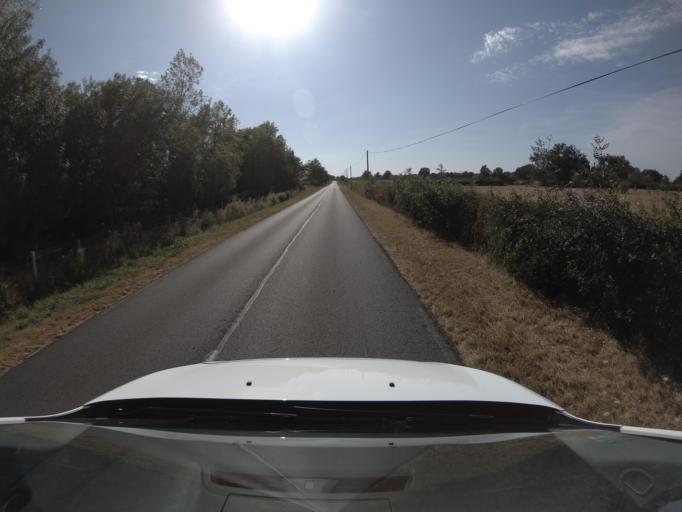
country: FR
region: Poitou-Charentes
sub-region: Departement des Deux-Sevres
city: Argenton-les-Vallees
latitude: 47.0006
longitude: -0.3914
